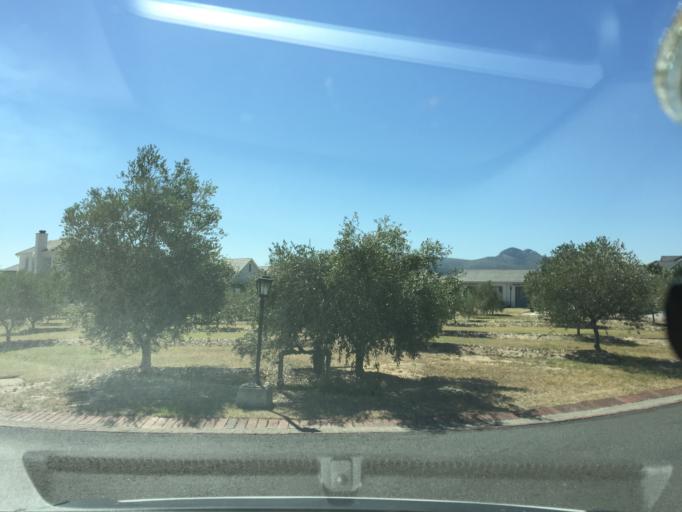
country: ZA
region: Western Cape
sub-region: Cape Winelands District Municipality
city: Paarl
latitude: -33.8020
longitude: 18.9737
